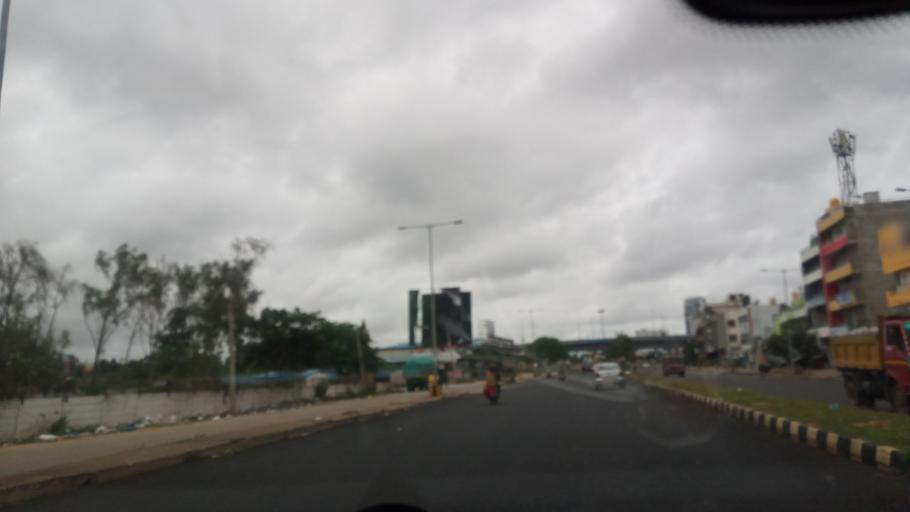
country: IN
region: Karnataka
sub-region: Mysore
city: Mysore
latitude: 12.3307
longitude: 76.5979
